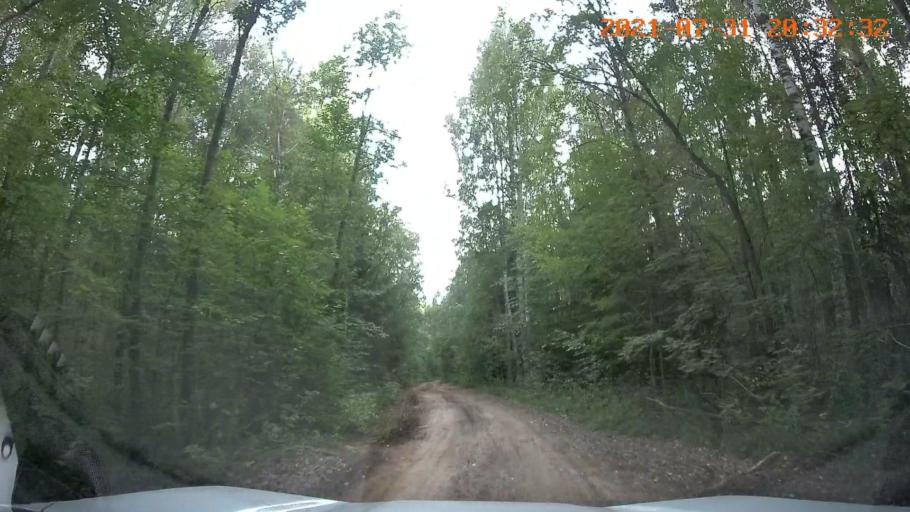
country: RU
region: Republic of Karelia
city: Shal'skiy
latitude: 61.6614
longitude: 36.2732
